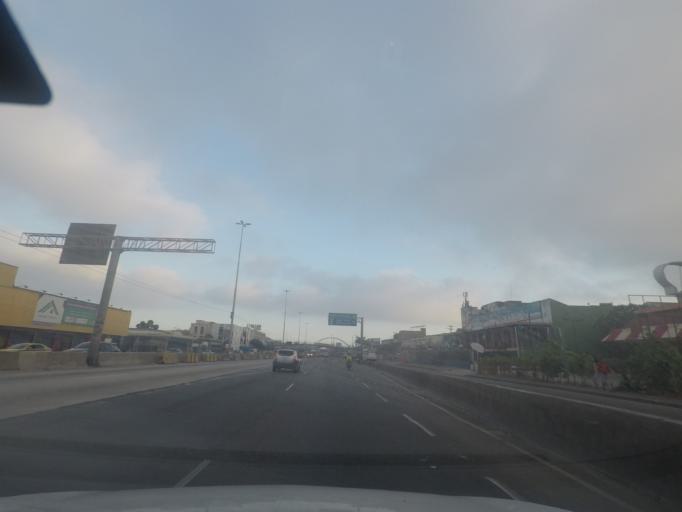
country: BR
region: Rio de Janeiro
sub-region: Rio De Janeiro
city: Rio de Janeiro
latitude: -22.8586
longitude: -43.2476
